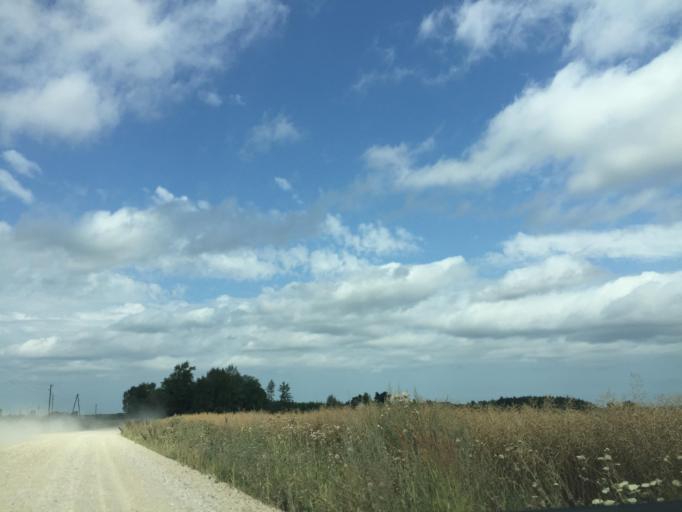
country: LV
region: Kandava
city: Kandava
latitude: 56.9867
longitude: 22.9045
